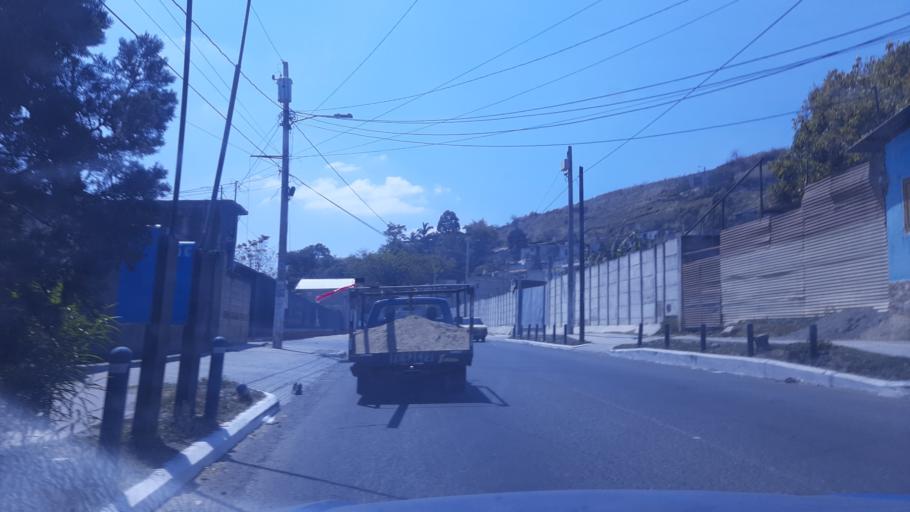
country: GT
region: Guatemala
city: Villa Nueva
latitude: 14.5177
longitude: -90.5932
